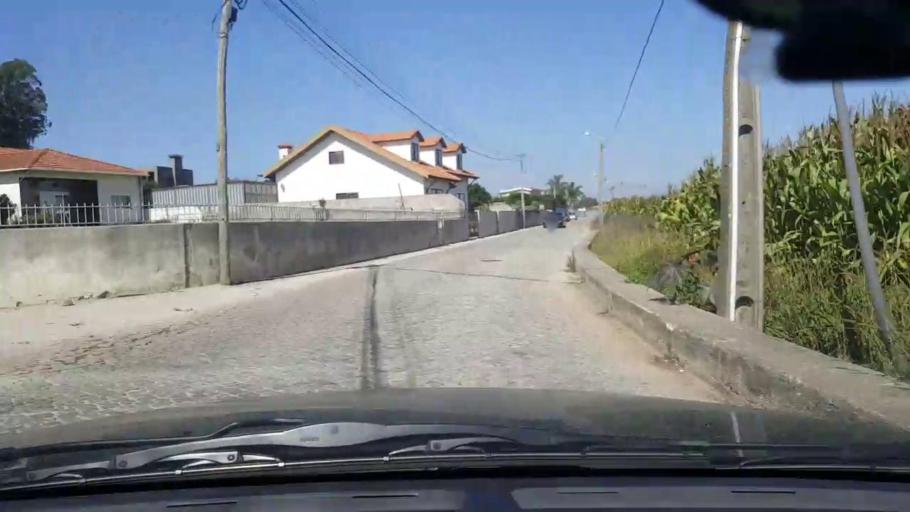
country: PT
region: Porto
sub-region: Matosinhos
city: Lavra
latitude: 41.2630
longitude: -8.6960
